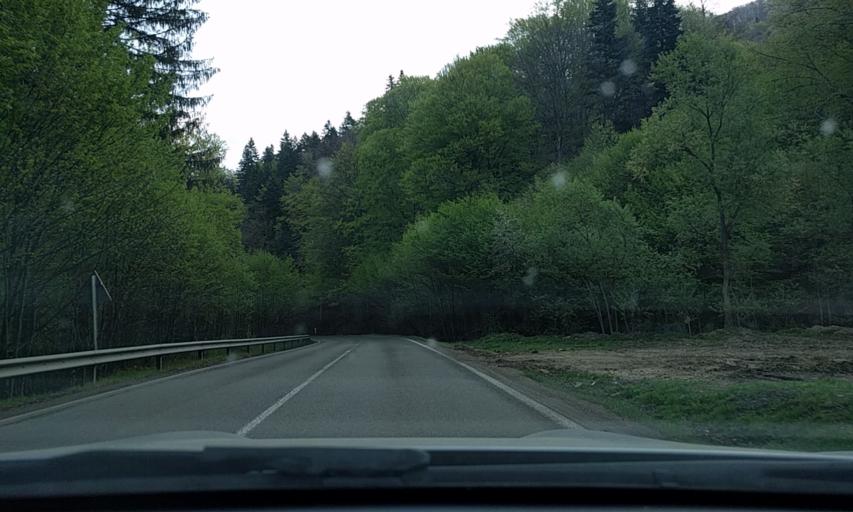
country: RO
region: Covasna
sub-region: Comuna Bretcu
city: Bretcu
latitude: 46.1050
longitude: 26.4107
